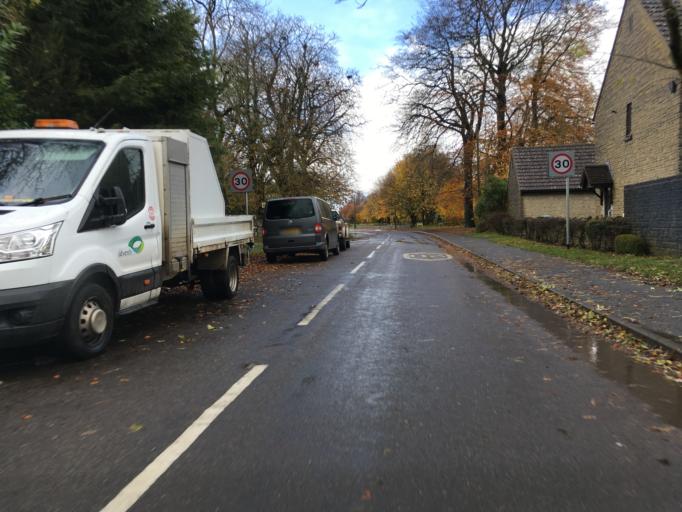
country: GB
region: England
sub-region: South Gloucestershire
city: Marshfield
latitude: 51.4629
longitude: -2.3122
